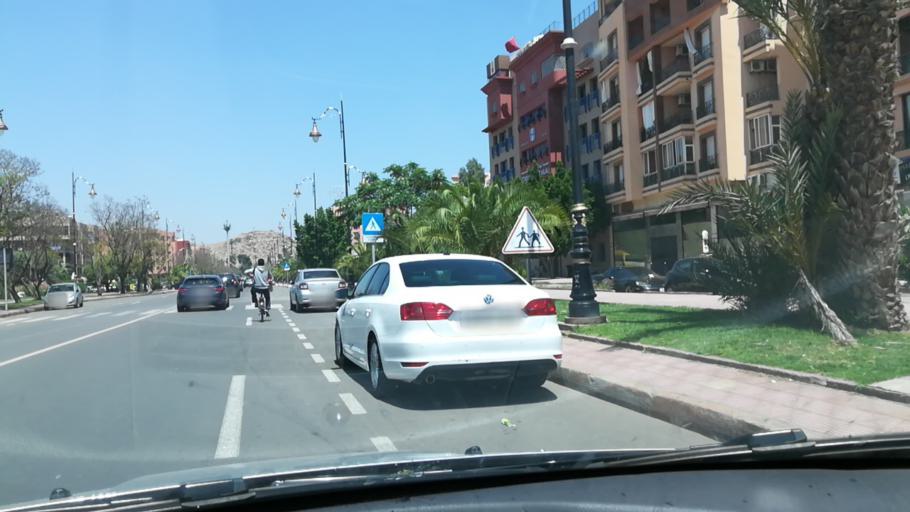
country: MA
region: Marrakech-Tensift-Al Haouz
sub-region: Marrakech
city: Marrakesh
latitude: 31.6361
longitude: -8.0200
